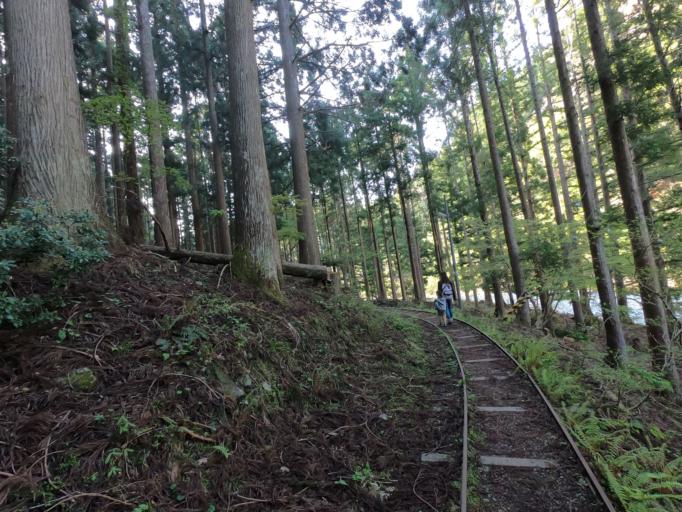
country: JP
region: Fukui
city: Obama
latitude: 35.3066
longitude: 135.7192
